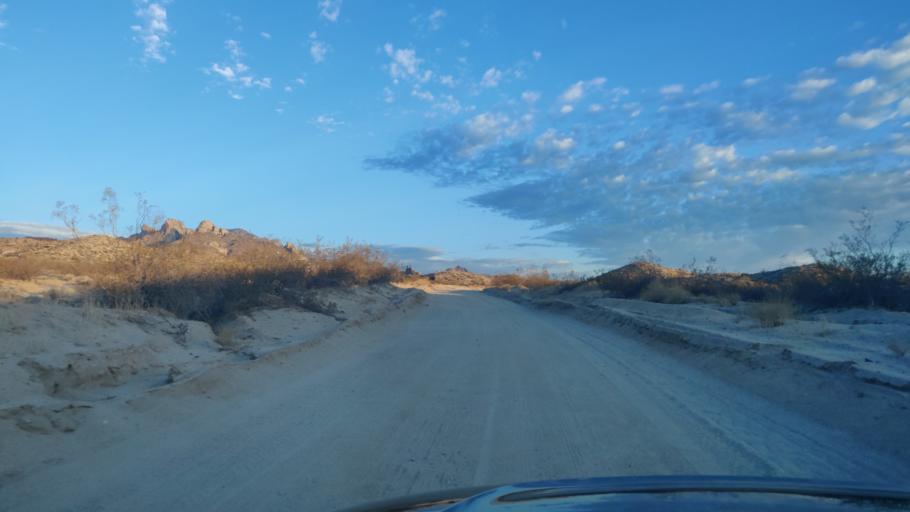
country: US
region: Nevada
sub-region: Clark County
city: Laughlin
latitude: 35.2117
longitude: -114.6747
